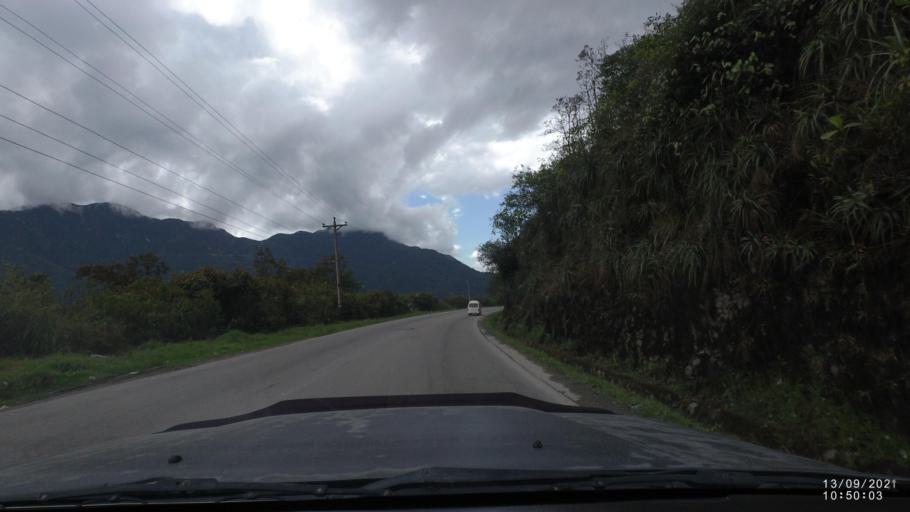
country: BO
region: Cochabamba
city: Colomi
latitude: -17.1954
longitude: -65.8547
